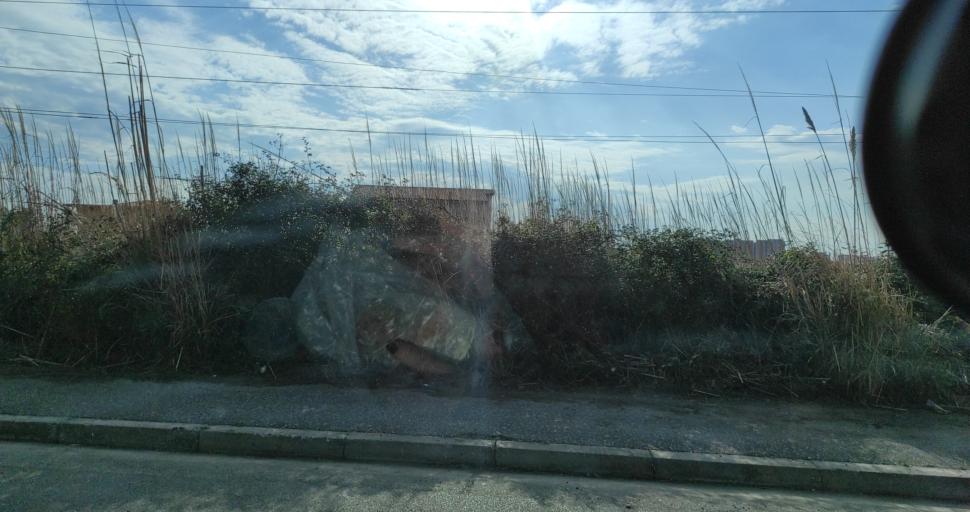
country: AL
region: Lezhe
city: Lezhe
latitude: 41.7978
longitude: 19.6188
